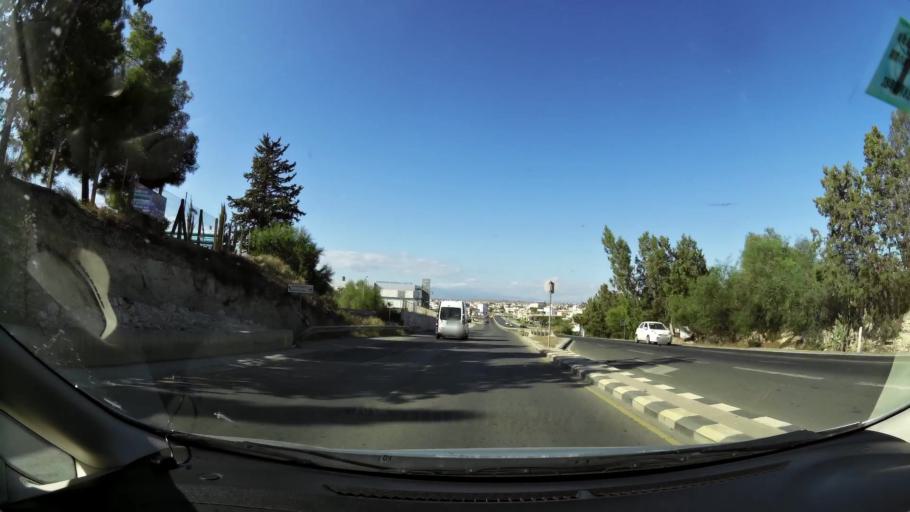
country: CY
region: Lefkosia
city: Tseri
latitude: 35.1231
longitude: 33.3434
